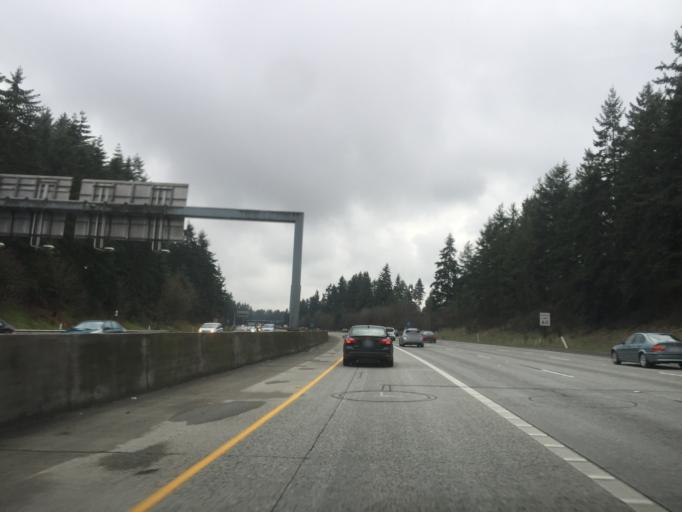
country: US
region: Washington
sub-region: Snohomish County
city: Mountlake Terrace
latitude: 47.7703
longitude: -122.3217
